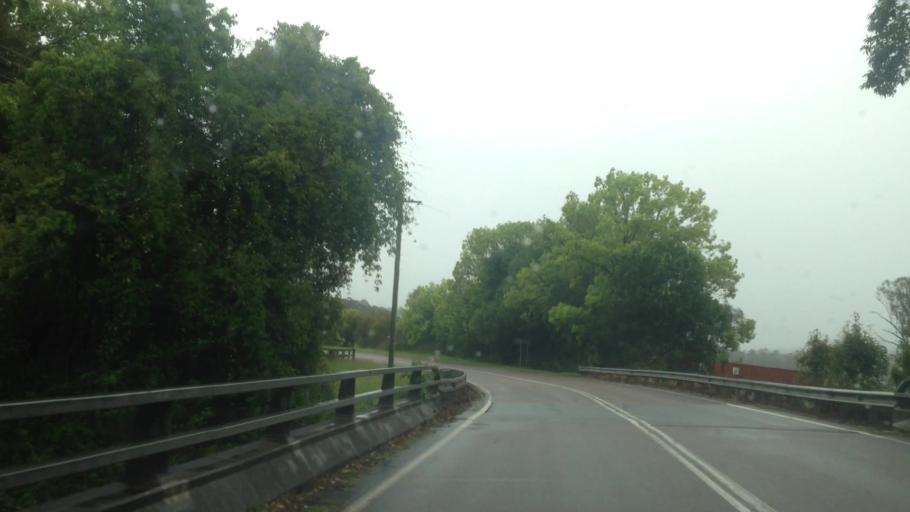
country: AU
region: New South Wales
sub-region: Wyong Shire
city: Little Jilliby
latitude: -33.2368
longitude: 151.3791
